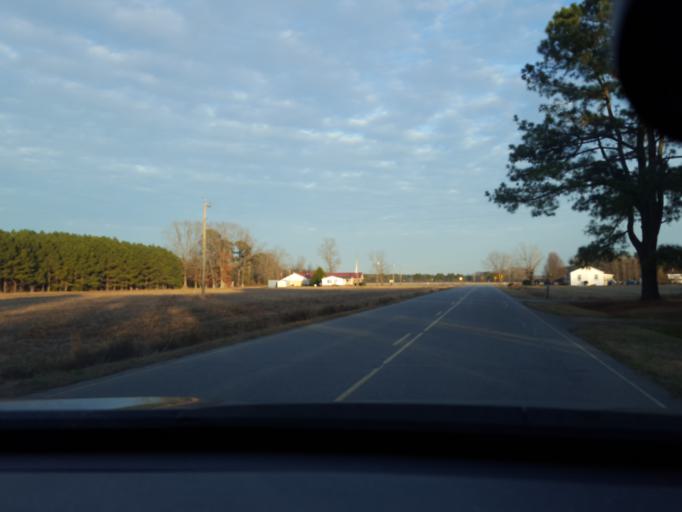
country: US
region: North Carolina
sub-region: Hertford County
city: Murfreesboro
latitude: 36.2716
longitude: -77.2263
